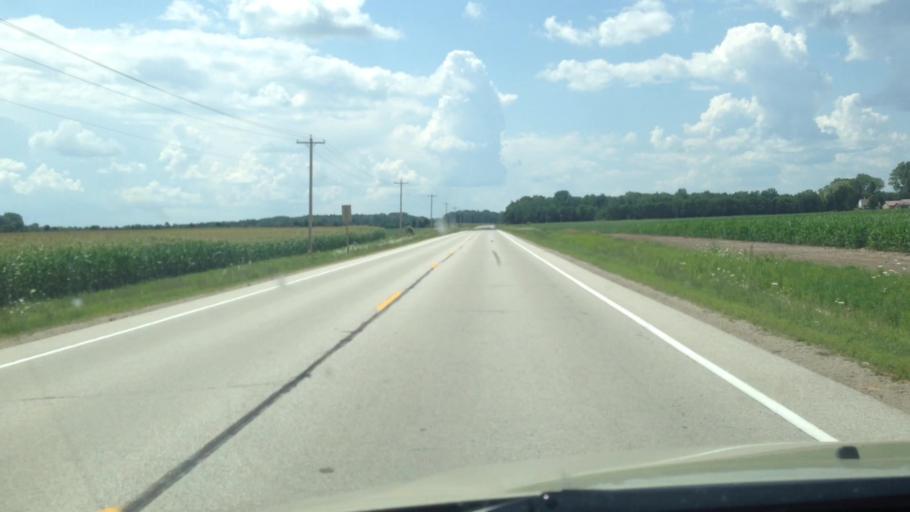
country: US
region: Wisconsin
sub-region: Brown County
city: Pulaski
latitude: 44.6458
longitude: -88.1631
